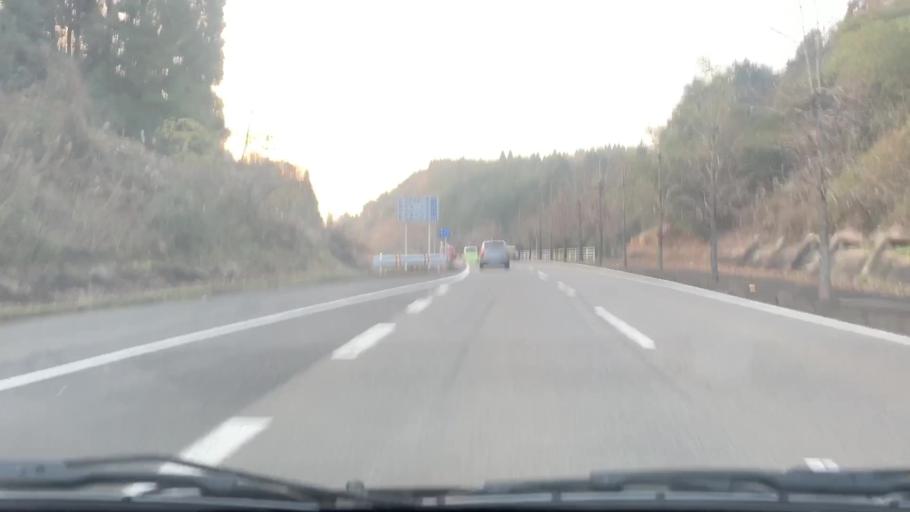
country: JP
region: Saga Prefecture
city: Imaricho-ko
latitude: 33.2656
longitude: 129.9565
